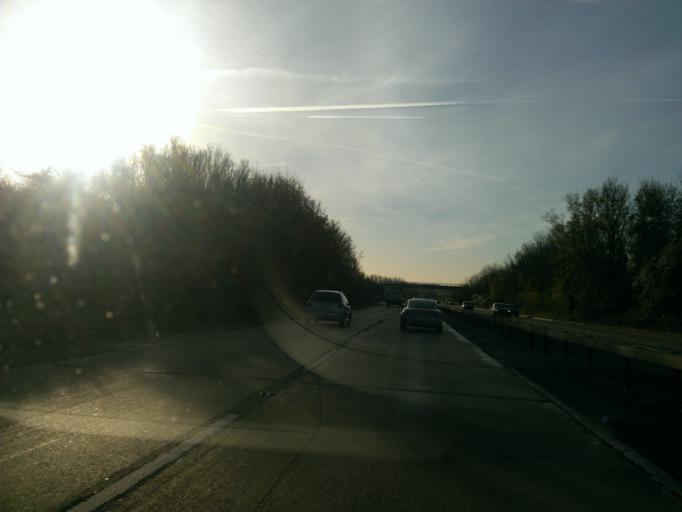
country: GB
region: England
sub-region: Essex
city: Kelvedon
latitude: 51.8460
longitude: 0.7242
